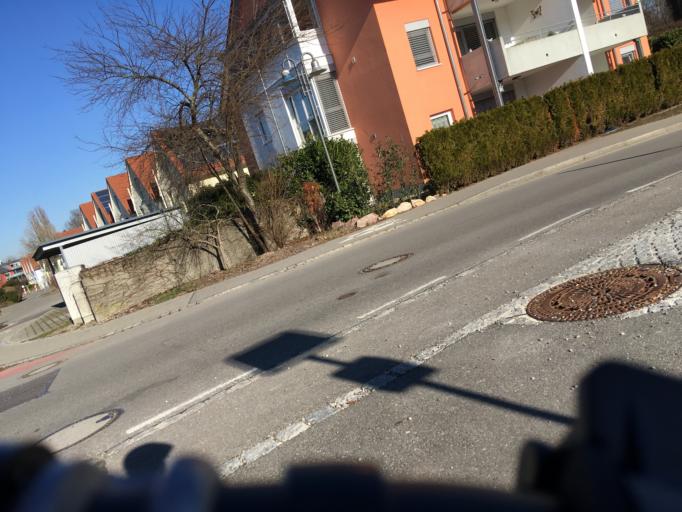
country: DE
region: Baden-Wuerttemberg
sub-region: Freiburg Region
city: Rielasingen-Worblingen
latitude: 47.7280
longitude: 8.8372
